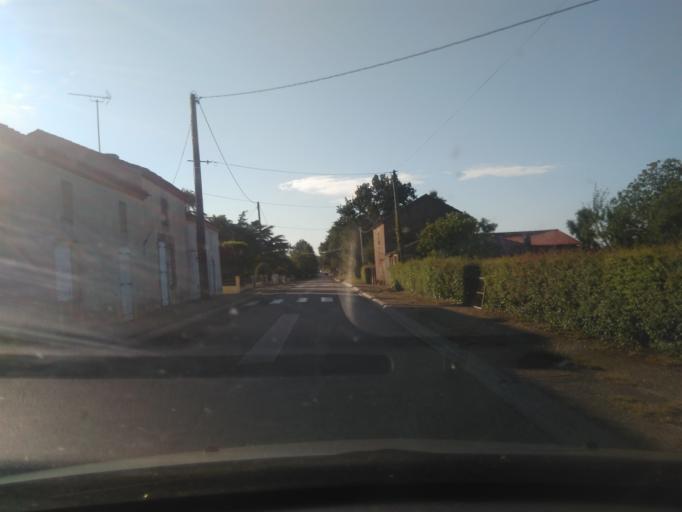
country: FR
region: Pays de la Loire
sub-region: Departement de la Vendee
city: Dompierre-sur-Yon
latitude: 46.7389
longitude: -1.4024
